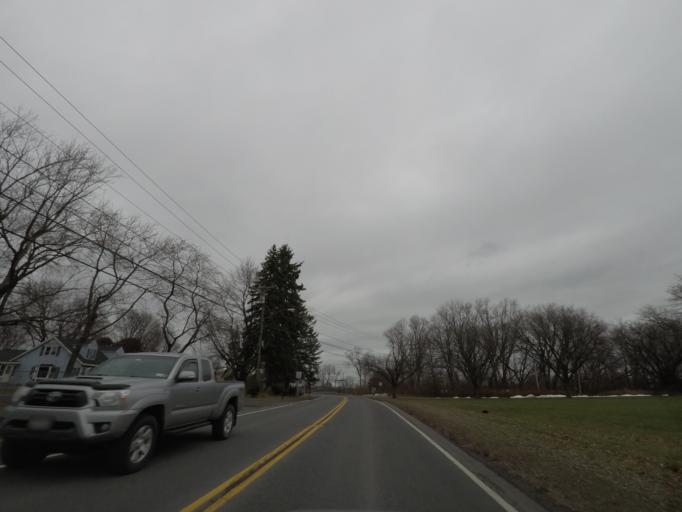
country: US
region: New York
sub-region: Albany County
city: Cohoes
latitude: 42.7582
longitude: -73.7540
